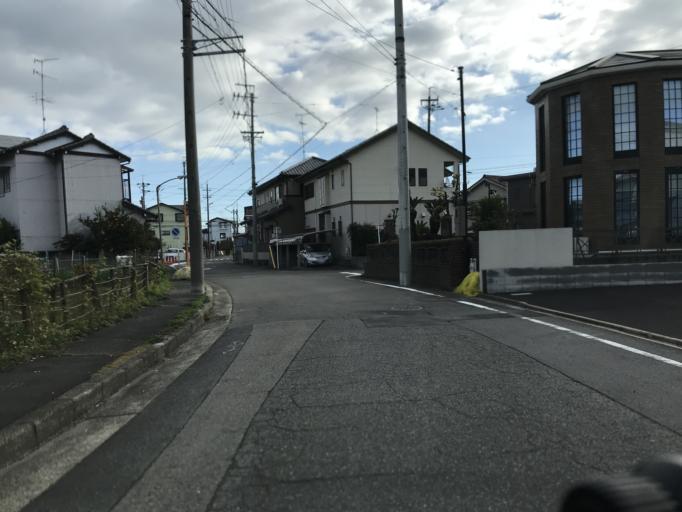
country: JP
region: Aichi
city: Nagoya-shi
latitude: 35.1948
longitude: 136.8441
